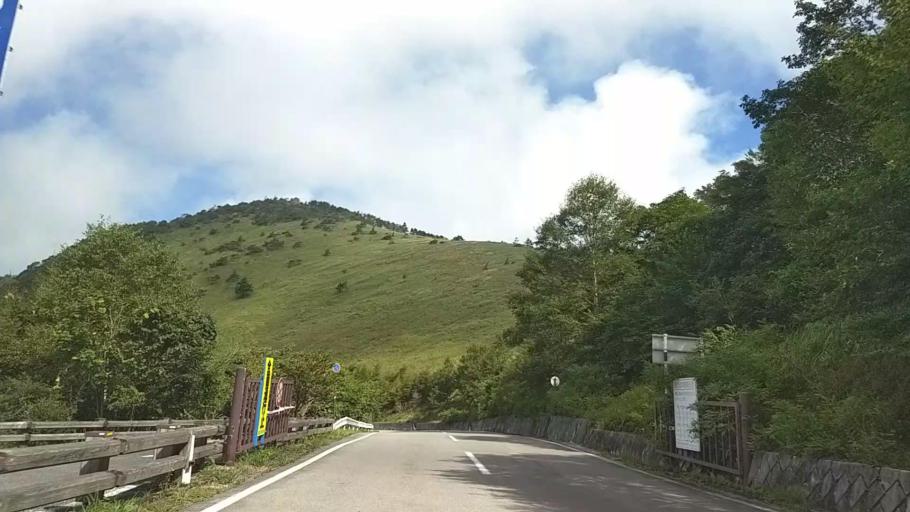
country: JP
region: Nagano
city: Suwa
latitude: 36.1208
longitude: 138.1598
